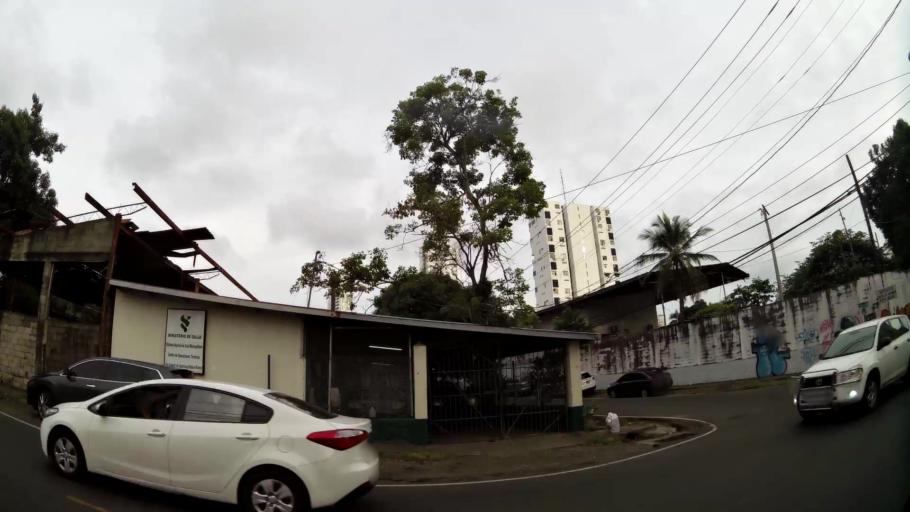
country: PA
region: Panama
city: Panama
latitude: 8.9960
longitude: -79.5164
